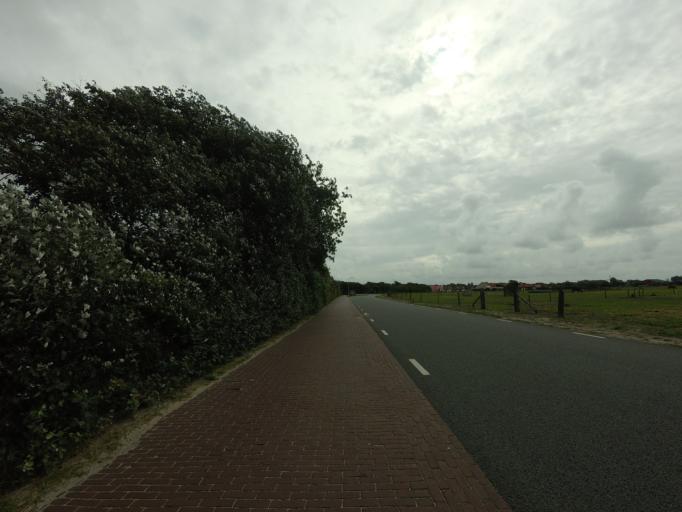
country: NL
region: Friesland
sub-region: Gemeente Ameland
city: Hollum
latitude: 53.4473
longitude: 5.6328
